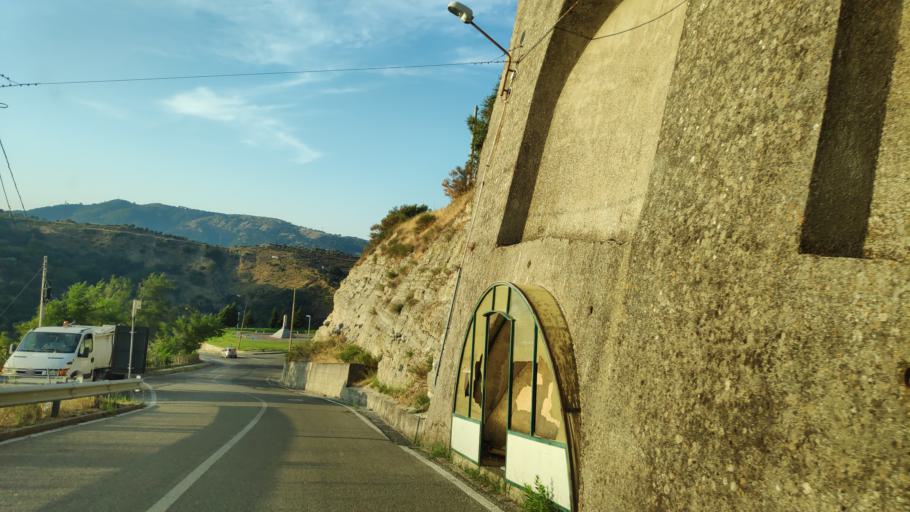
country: IT
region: Calabria
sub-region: Provincia di Catanzaro
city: Satriano
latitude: 38.6688
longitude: 16.4813
